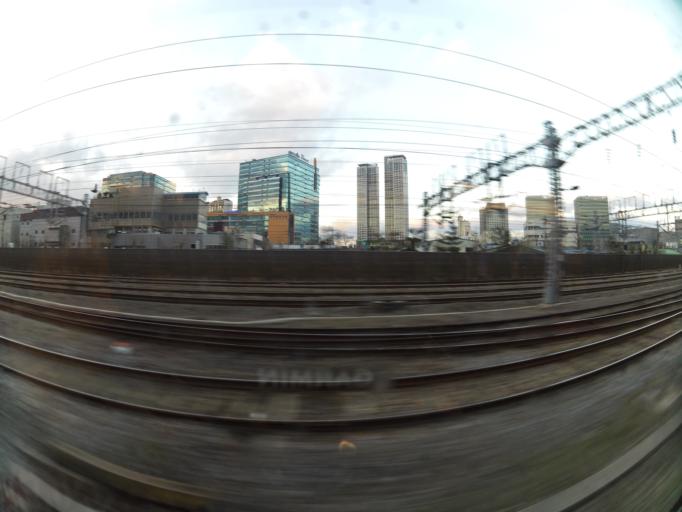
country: KR
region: Gyeonggi-do
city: Kwangmyong
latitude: 37.5129
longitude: 126.9012
